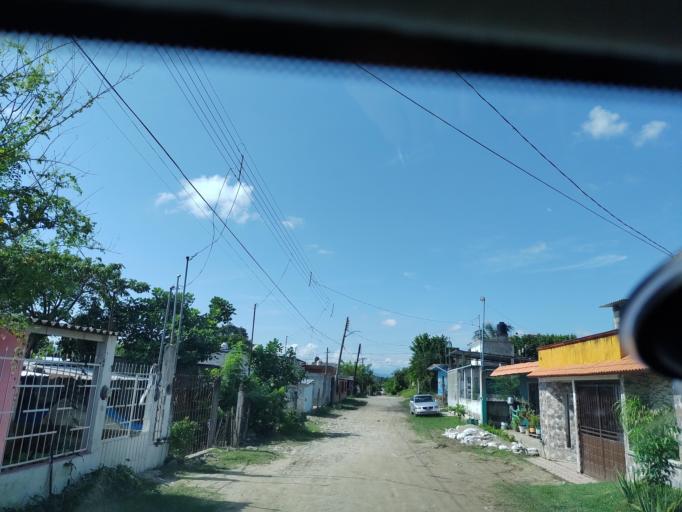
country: MX
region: Veracruz
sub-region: Martinez de la Torre
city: El Progreso
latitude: 20.1150
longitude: -97.0115
